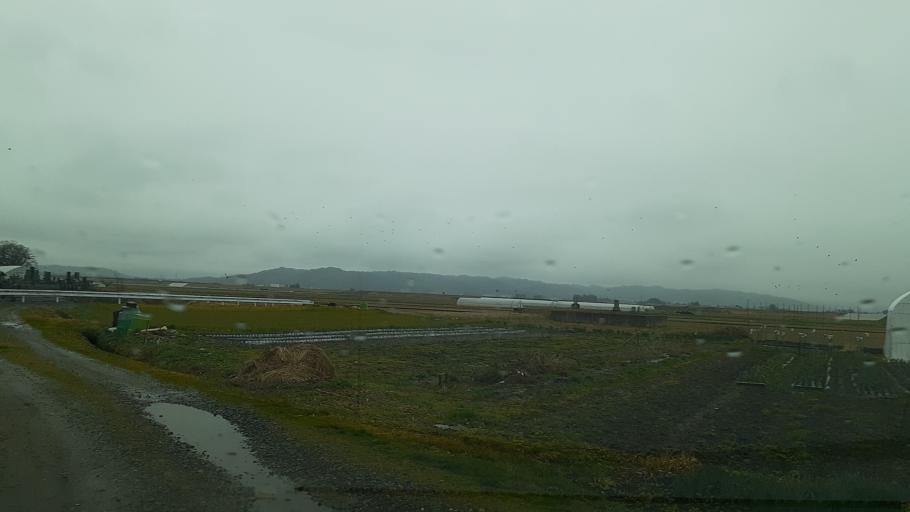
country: JP
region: Fukushima
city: Kitakata
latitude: 37.5850
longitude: 139.8568
